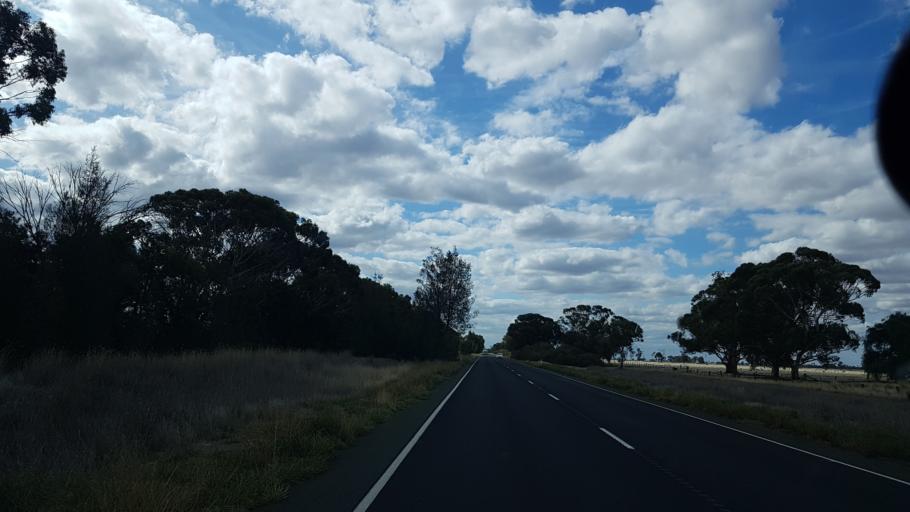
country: AU
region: Victoria
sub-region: Swan Hill
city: Swan Hill
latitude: -35.9824
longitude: 143.9452
